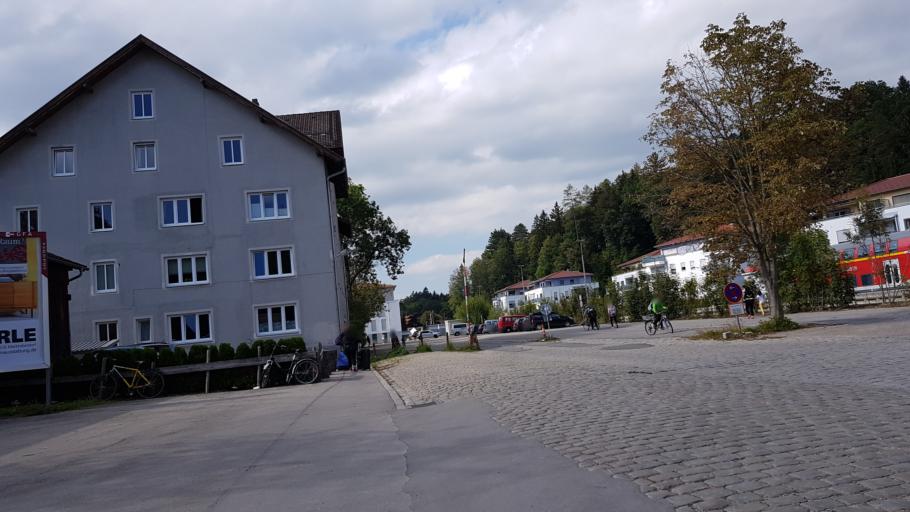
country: DE
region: Bavaria
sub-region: Swabia
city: Fuessen
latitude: 47.5704
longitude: 10.6969
